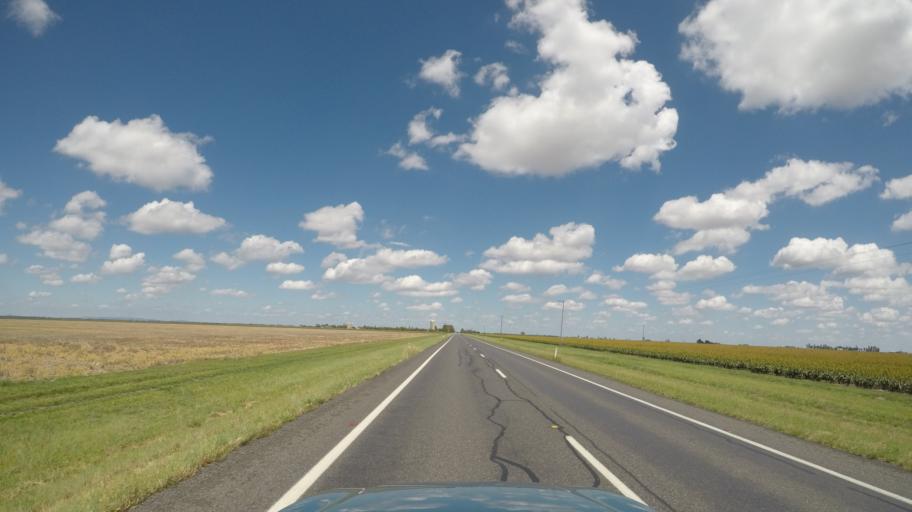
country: AU
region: Queensland
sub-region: Toowoomba
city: Oakey
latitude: -27.7580
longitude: 151.4714
